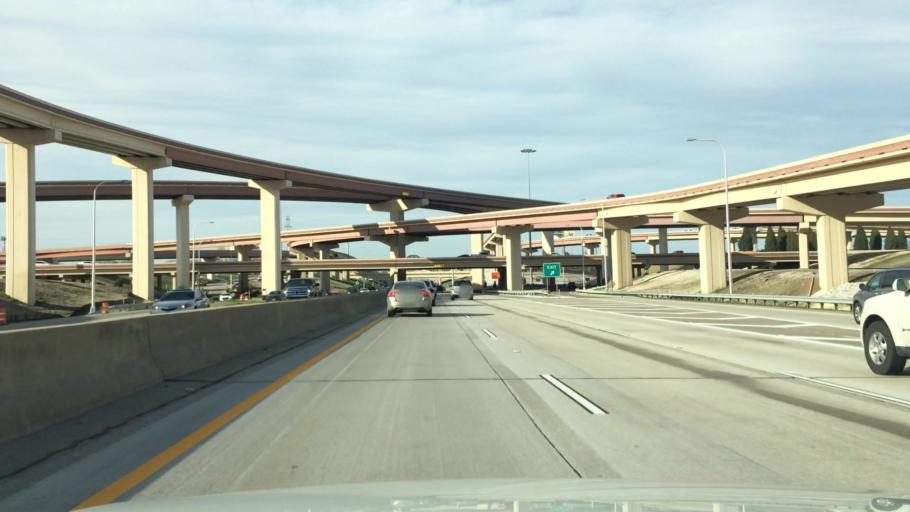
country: US
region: Texas
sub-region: Dallas County
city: Addison
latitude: 33.0110
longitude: -96.8291
